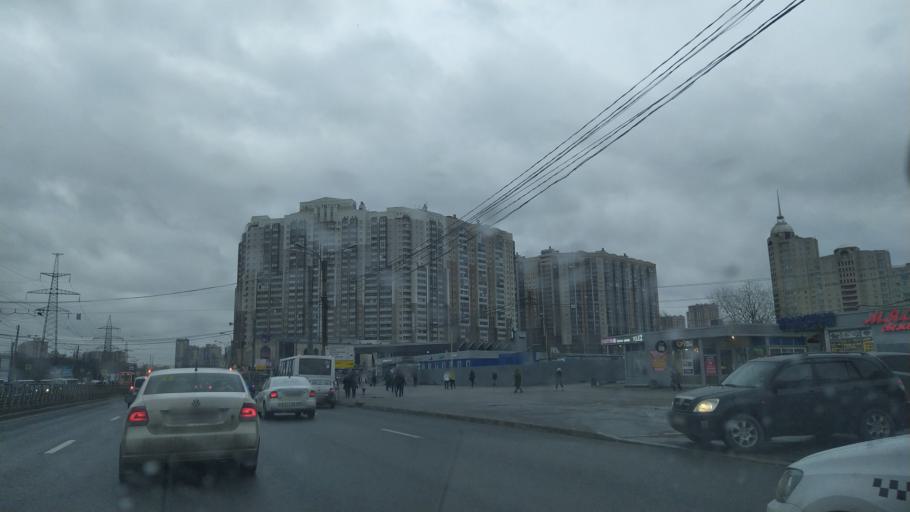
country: RU
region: St.-Petersburg
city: Novaya Derevnya
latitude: 60.0034
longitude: 30.2943
